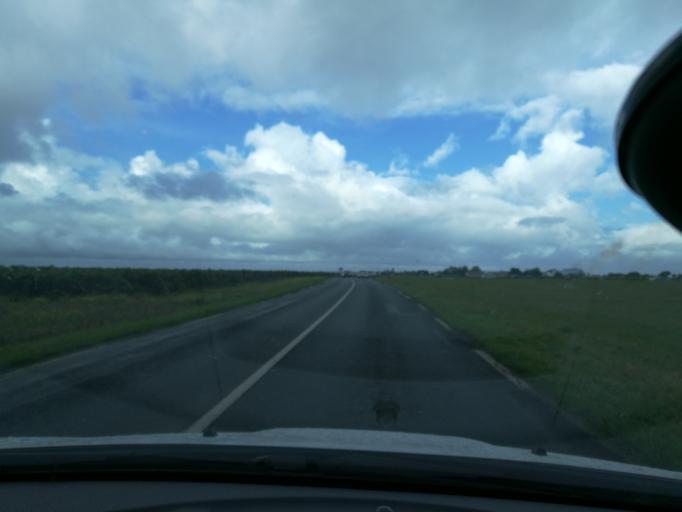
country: FR
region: Poitou-Charentes
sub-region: Departement de la Charente-Maritime
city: Saint-Martin-de-Re
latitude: 46.1977
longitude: -1.3689
